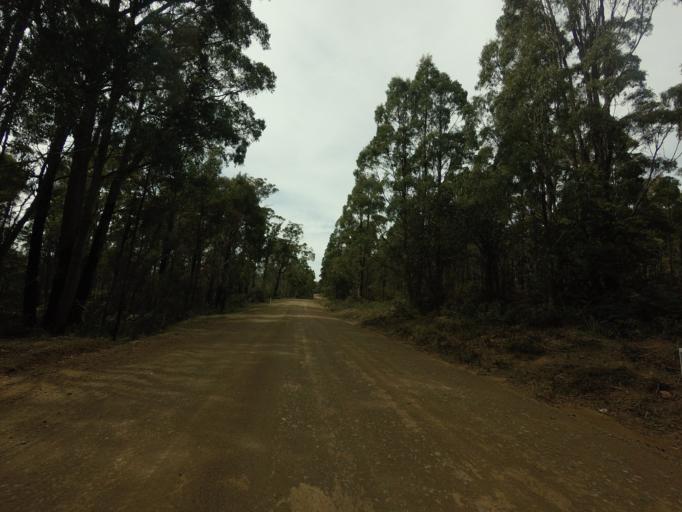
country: AU
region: Tasmania
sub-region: Sorell
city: Sorell
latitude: -42.4933
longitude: 147.6253
